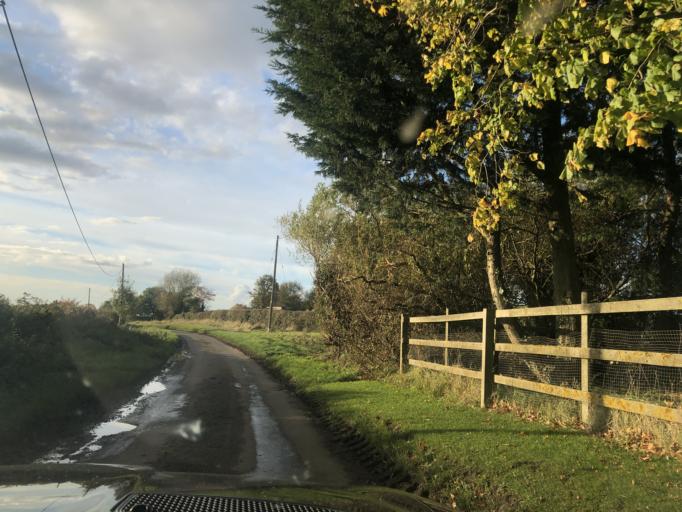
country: GB
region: England
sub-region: Warwickshire
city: Harbury
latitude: 52.2240
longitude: -1.4884
